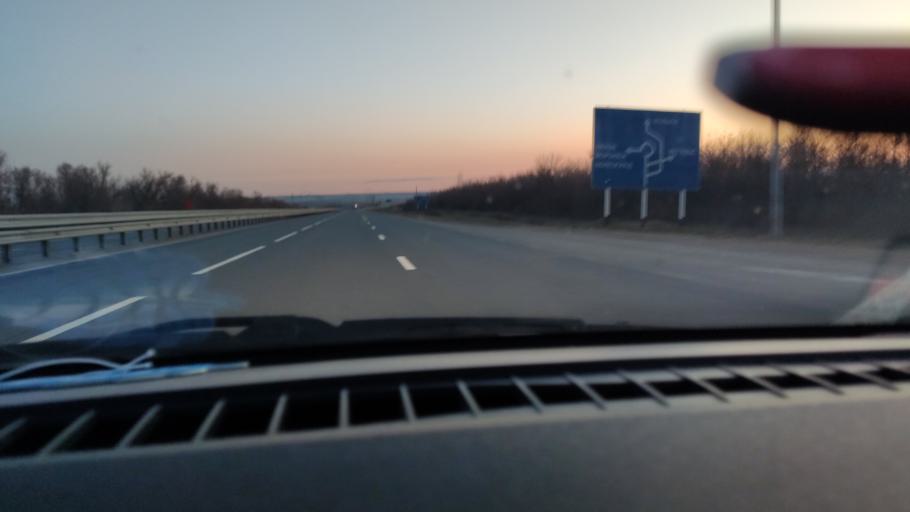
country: RU
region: Saratov
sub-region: Saratovskiy Rayon
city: Saratov
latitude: 51.6612
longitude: 45.9993
